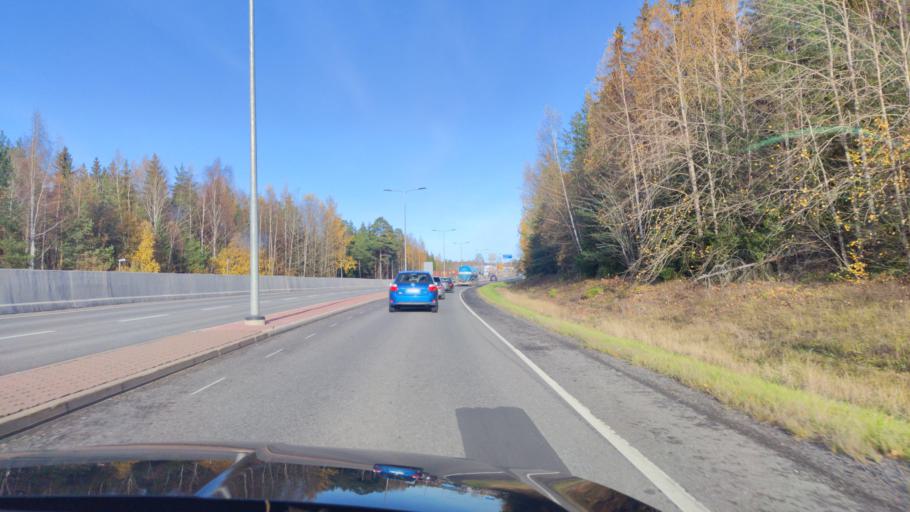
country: FI
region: Varsinais-Suomi
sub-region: Turku
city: Kaarina
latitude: 60.4260
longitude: 22.3807
